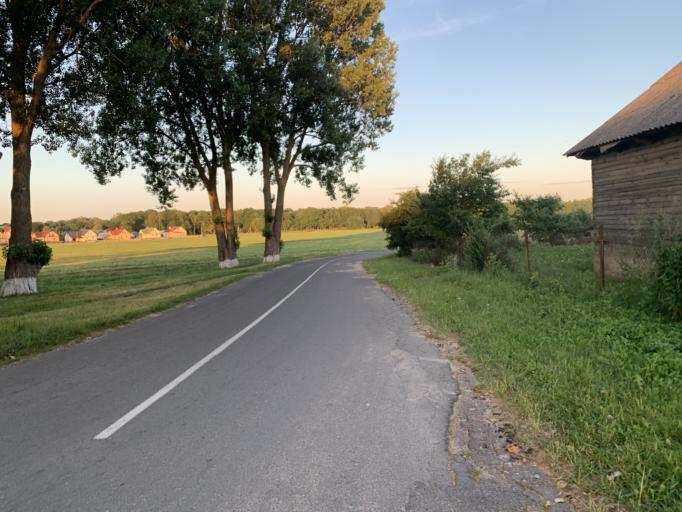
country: BY
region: Minsk
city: Nyasvizh
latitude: 53.2287
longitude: 26.6829
